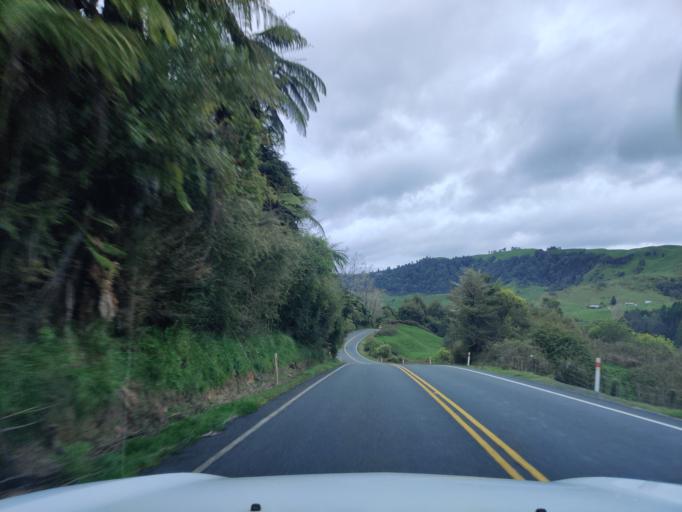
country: NZ
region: Waikato
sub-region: Otorohanga District
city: Otorohanga
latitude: -38.4963
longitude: 175.1893
